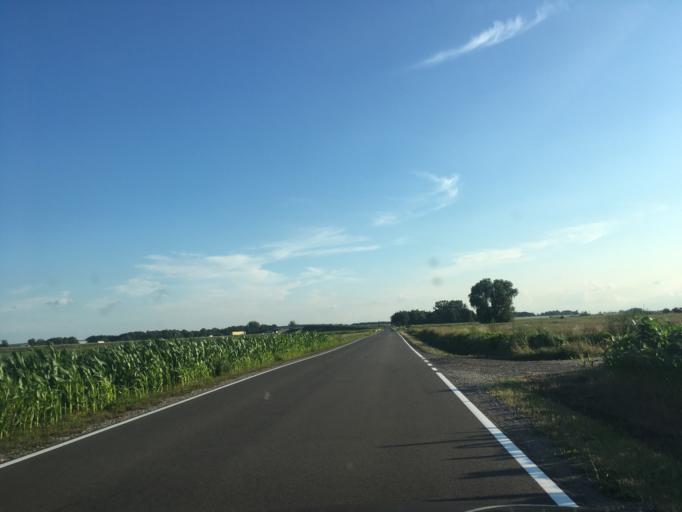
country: PL
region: Masovian Voivodeship
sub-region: Powiat warszawski zachodni
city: Bieniewice
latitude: 52.1476
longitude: 20.6013
